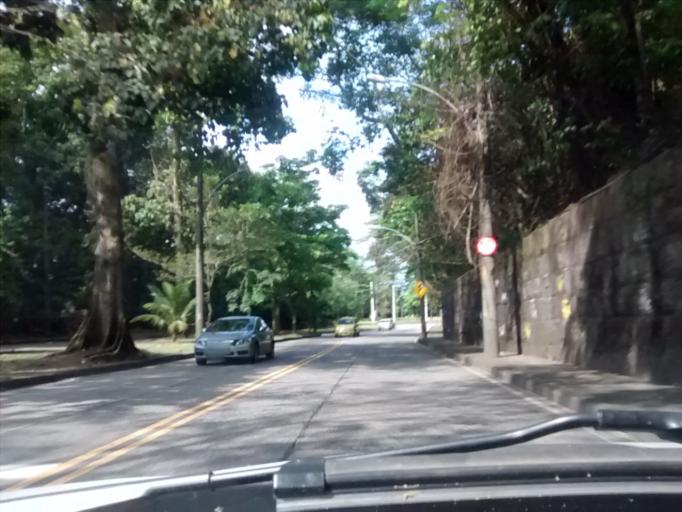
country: BR
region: Rio de Janeiro
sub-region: Rio De Janeiro
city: Rio de Janeiro
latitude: -22.9588
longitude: -43.2675
